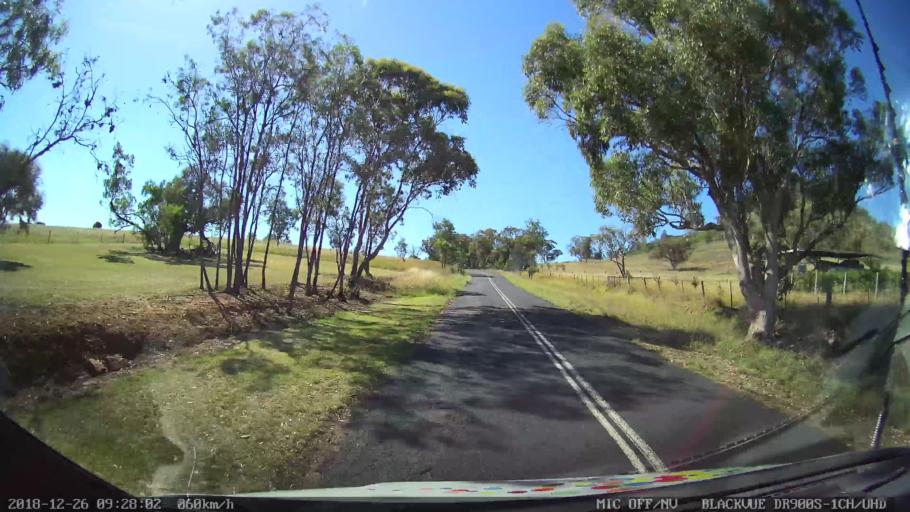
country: AU
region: New South Wales
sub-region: Mid-Western Regional
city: Kandos
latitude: -32.8417
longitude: 150.0199
